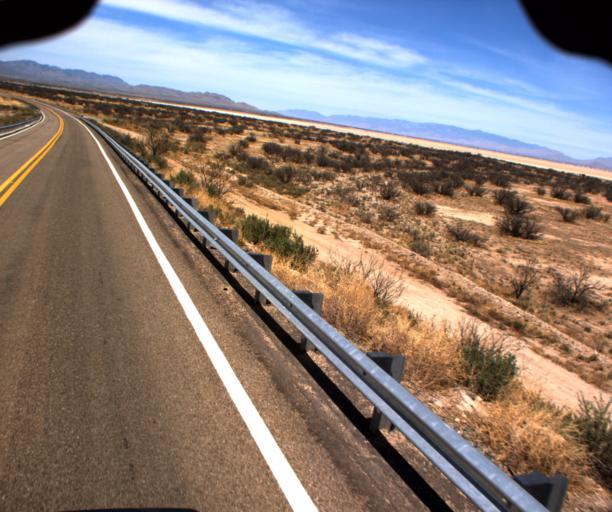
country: US
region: Arizona
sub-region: Cochise County
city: Willcox
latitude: 32.1331
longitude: -109.9106
